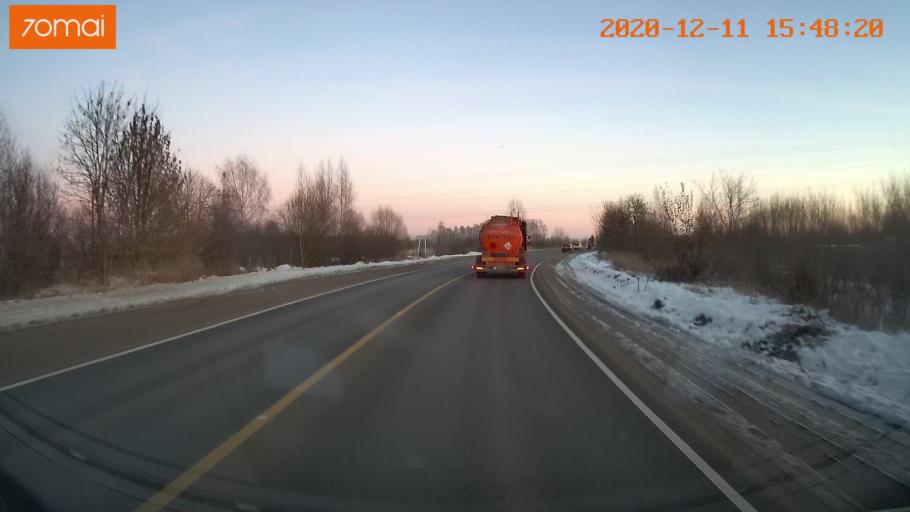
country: RU
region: Ivanovo
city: Novo-Talitsy
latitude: 56.9930
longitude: 40.8668
